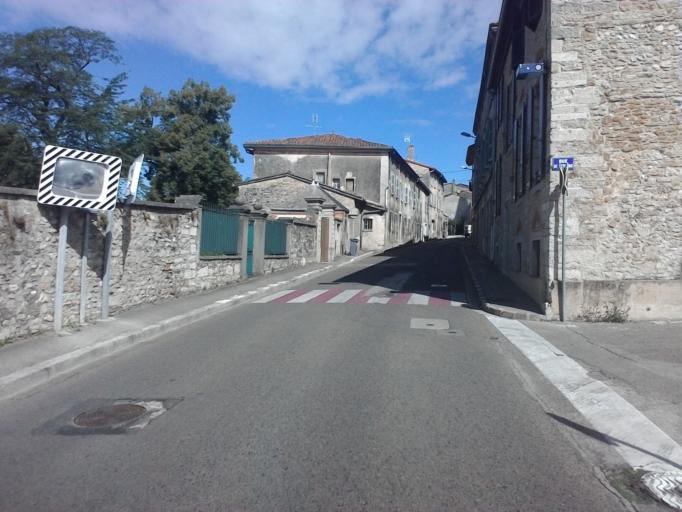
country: FR
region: Rhone-Alpes
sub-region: Departement de l'Ain
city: Amberieu-en-Bugey
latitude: 45.9568
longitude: 5.3597
